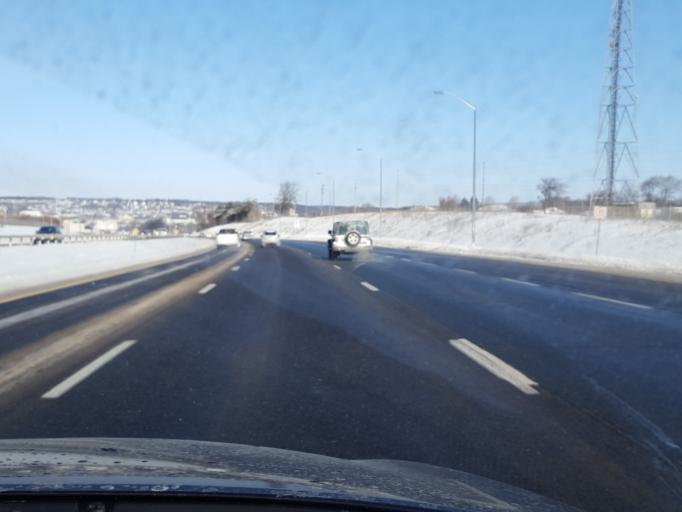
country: CA
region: Ontario
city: Barrie
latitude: 44.3547
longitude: -79.6899
